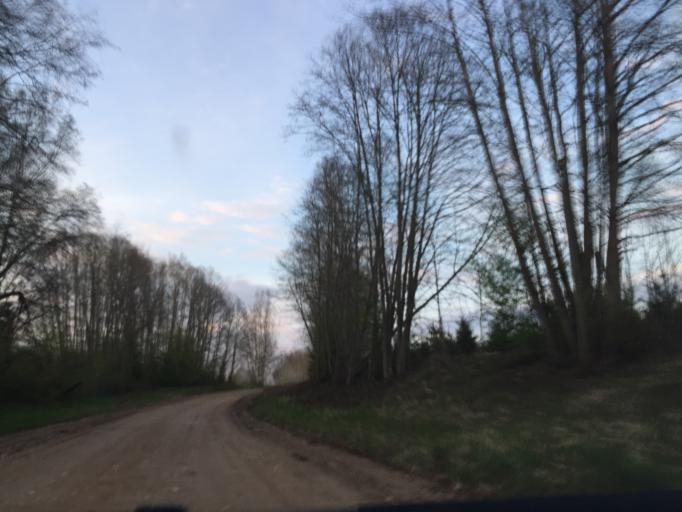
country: LV
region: Aluksnes Rajons
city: Aluksne
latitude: 57.3124
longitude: 26.9165
